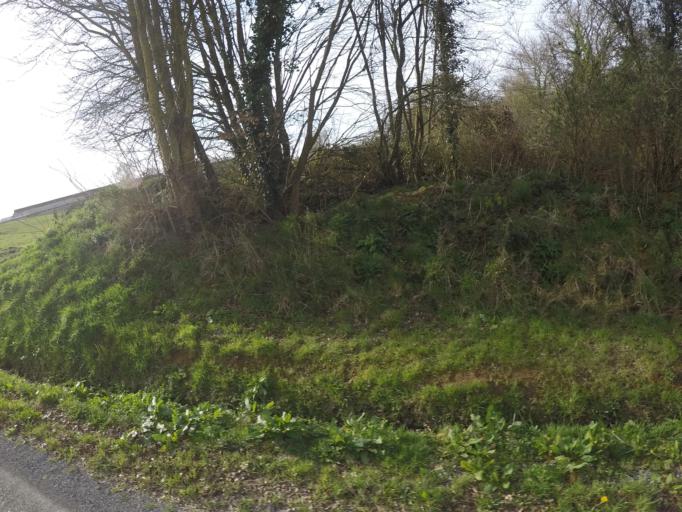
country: FR
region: Brittany
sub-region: Departement des Cotes-d'Armor
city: Plelo
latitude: 48.5258
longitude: -2.9650
